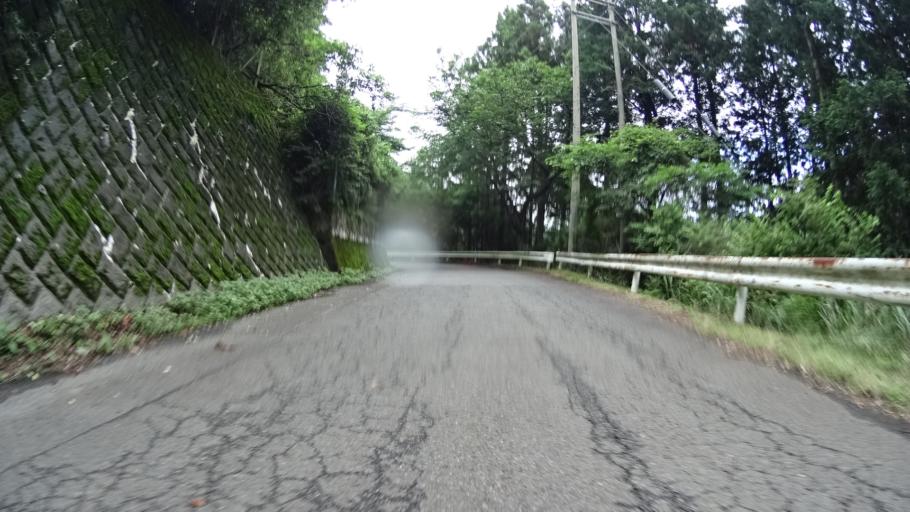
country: JP
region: Kanagawa
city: Hadano
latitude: 35.4797
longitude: 139.2113
